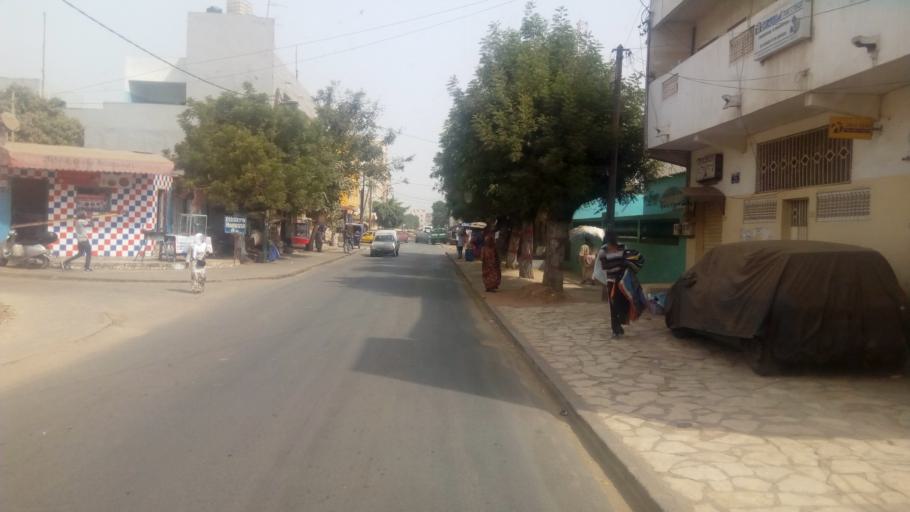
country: SN
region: Dakar
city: Grand Dakar
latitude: 14.7257
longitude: -17.4527
